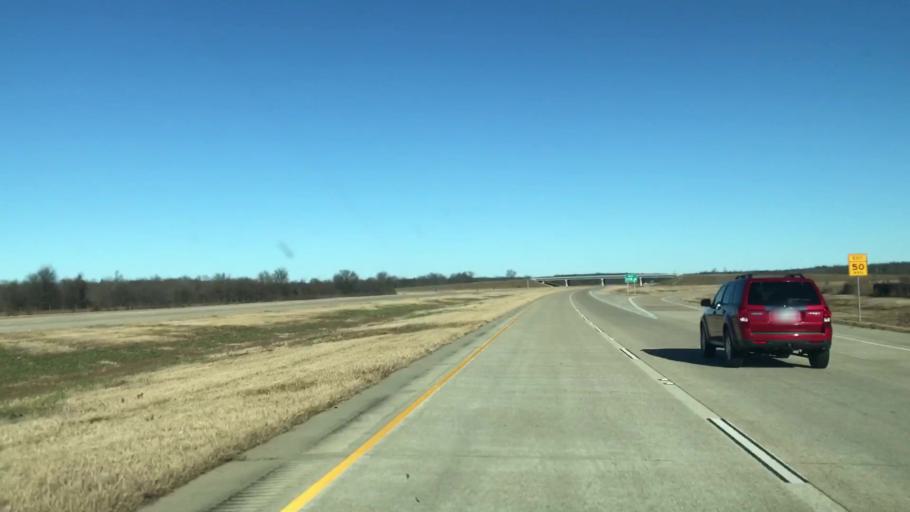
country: US
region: Louisiana
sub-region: Caddo Parish
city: Oil City
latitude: 32.7616
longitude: -93.8864
